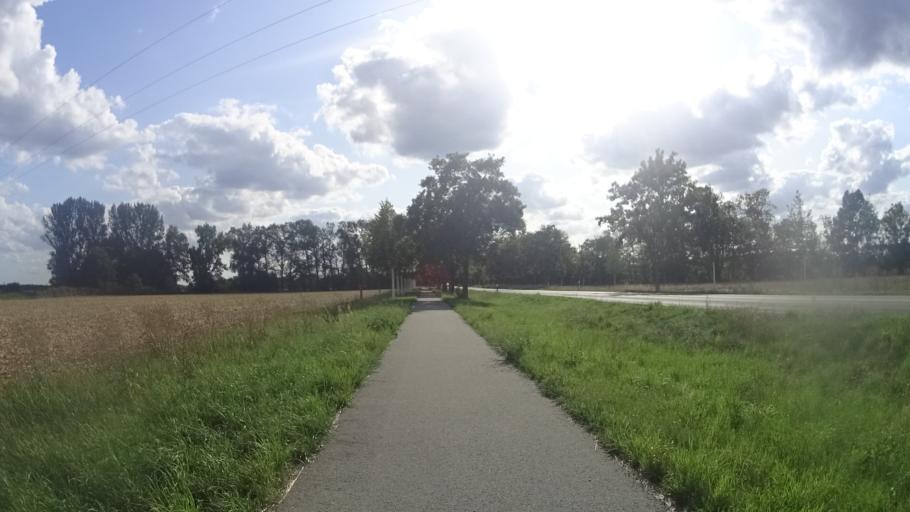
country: DE
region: Brandenburg
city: Rathenow
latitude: 52.6507
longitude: 12.3358
